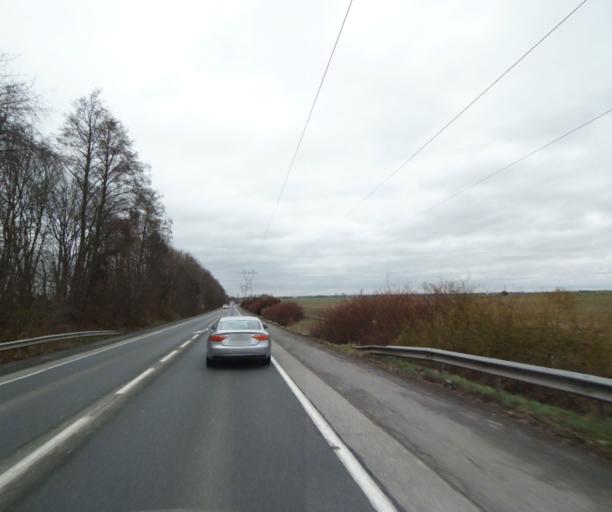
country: FR
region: Nord-Pas-de-Calais
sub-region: Departement du Nord
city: Saint-Saulve
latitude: 50.3630
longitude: 3.5649
